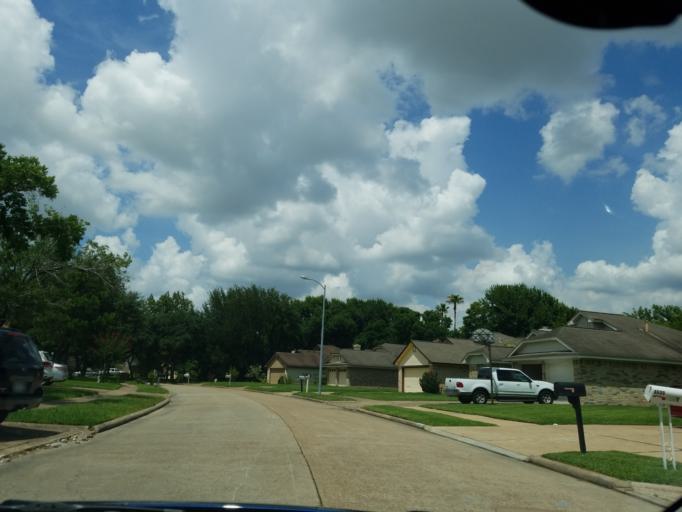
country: US
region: Texas
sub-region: Harris County
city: Cypress
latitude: 29.8725
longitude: -95.7308
